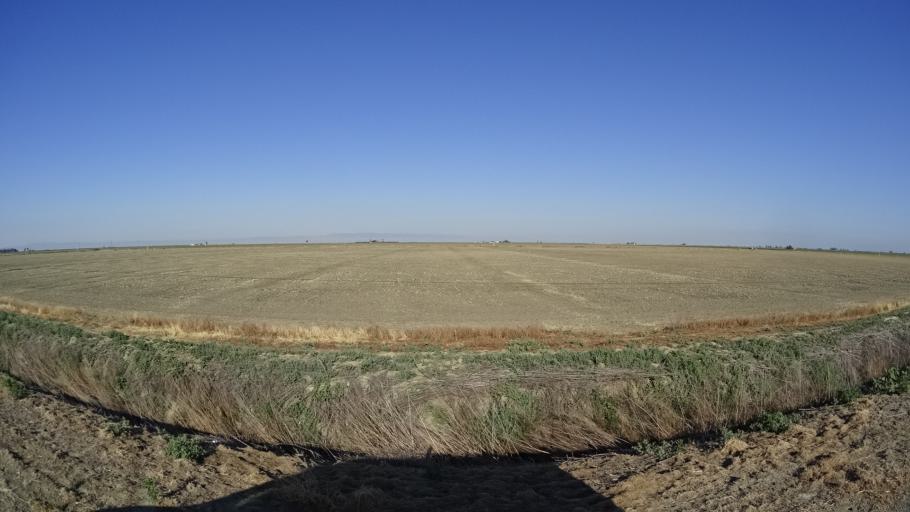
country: US
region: California
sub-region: Fresno County
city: Riverdale
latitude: 36.3975
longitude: -119.9277
